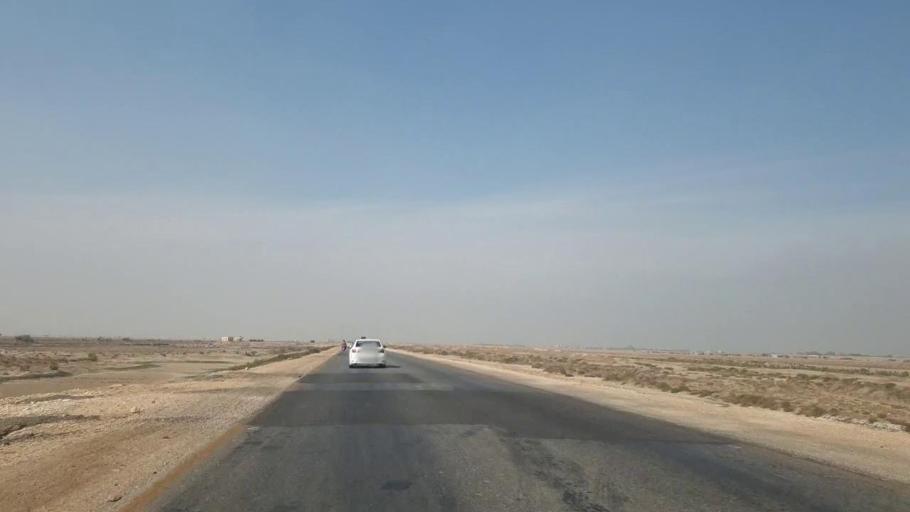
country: PK
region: Sindh
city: Sann
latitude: 25.8857
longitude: 68.2438
